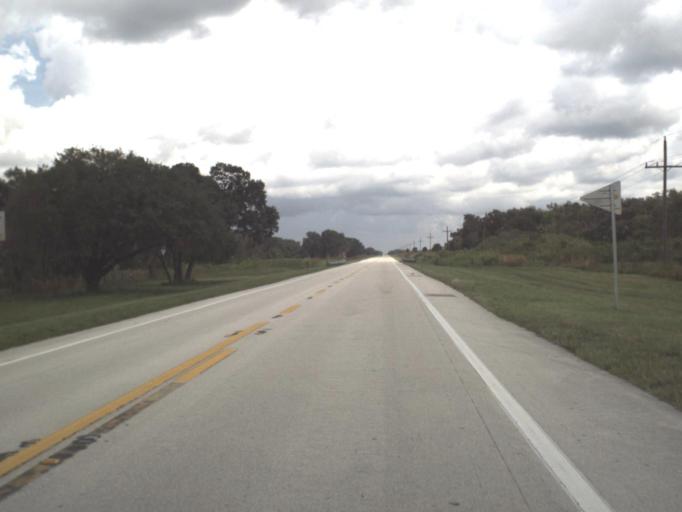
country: US
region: Florida
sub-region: Hendry County
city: Port LaBelle
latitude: 26.8149
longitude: -81.4107
